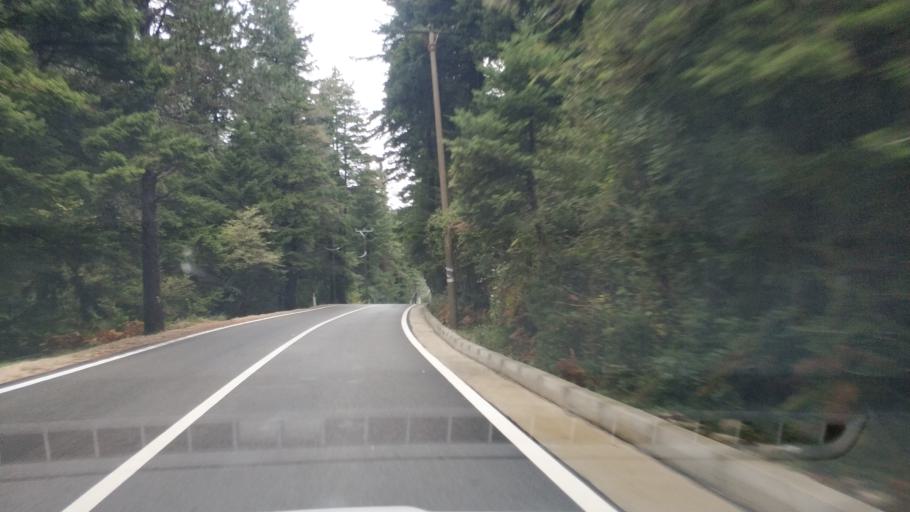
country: AL
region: Vlore
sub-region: Rrethi i Vlores
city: Brataj
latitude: 40.2084
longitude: 19.5806
